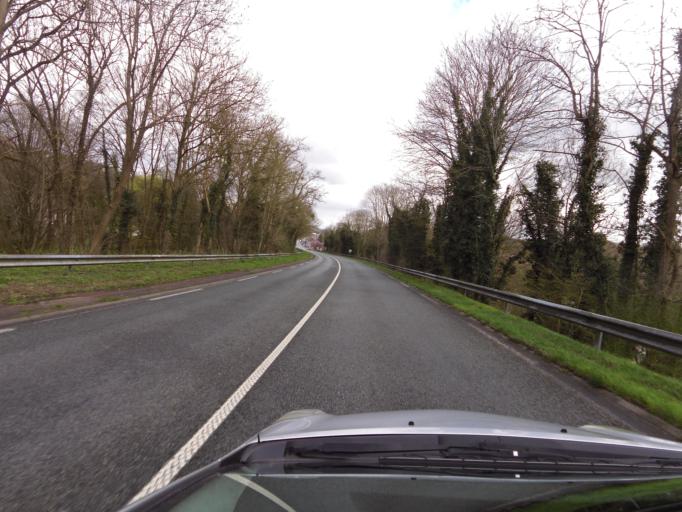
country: FR
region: Picardie
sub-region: Departement de l'Oise
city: Pont-Sainte-Maxence
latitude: 49.2901
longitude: 2.6047
